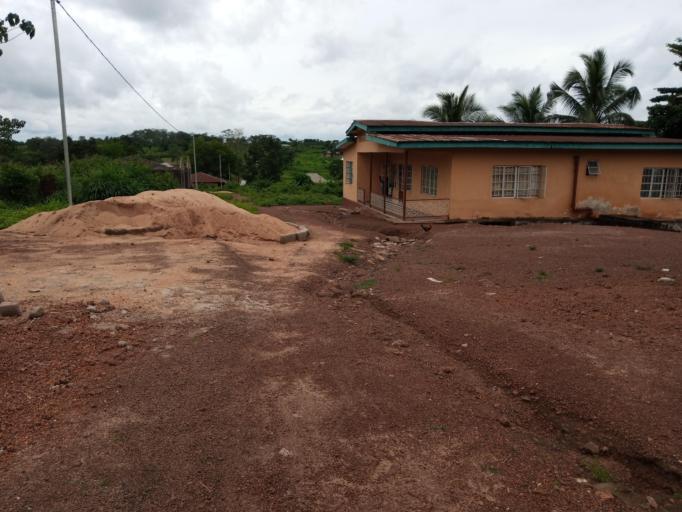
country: SL
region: Southern Province
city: Largo
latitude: 8.2009
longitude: -12.0572
